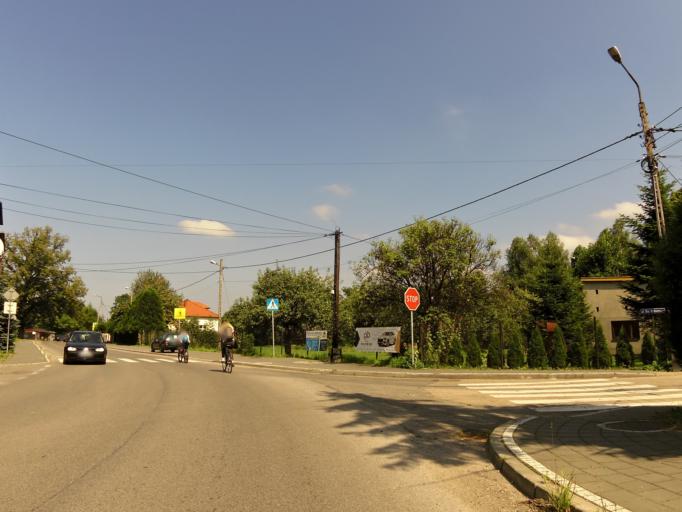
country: PL
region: Silesian Voivodeship
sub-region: Powiat zywiecki
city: Ciecina
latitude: 49.6169
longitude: 19.1375
